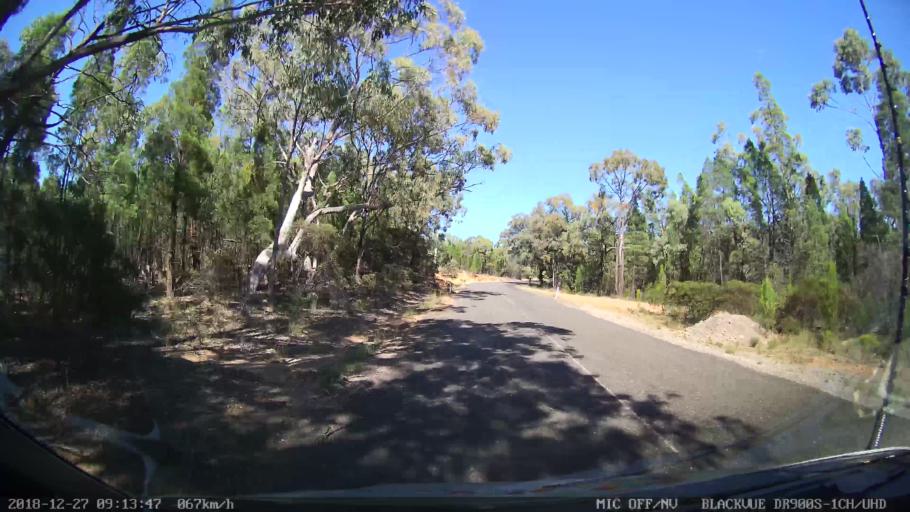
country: AU
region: New South Wales
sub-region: Lithgow
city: Portland
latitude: -33.1377
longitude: 150.0898
